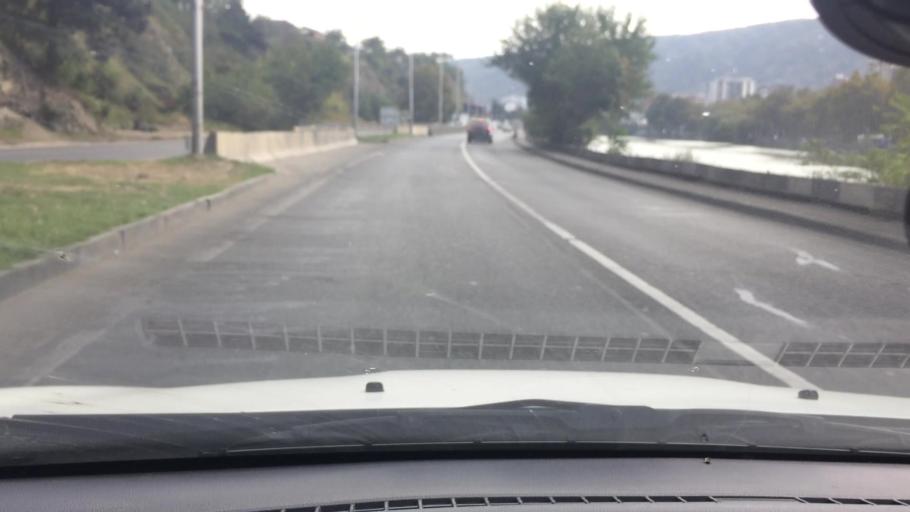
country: GE
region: T'bilisi
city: Tbilisi
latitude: 41.6884
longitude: 44.8206
